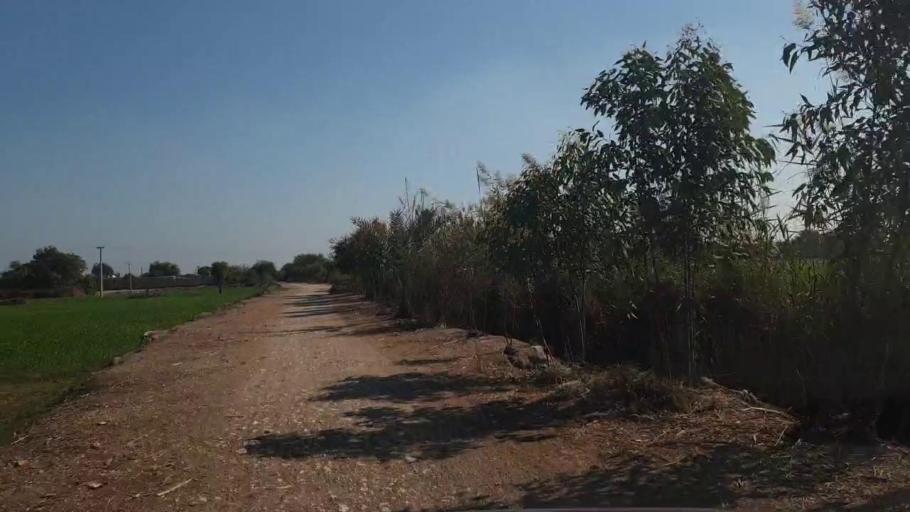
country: PK
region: Sindh
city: Shahdadpur
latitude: 25.9159
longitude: 68.5831
